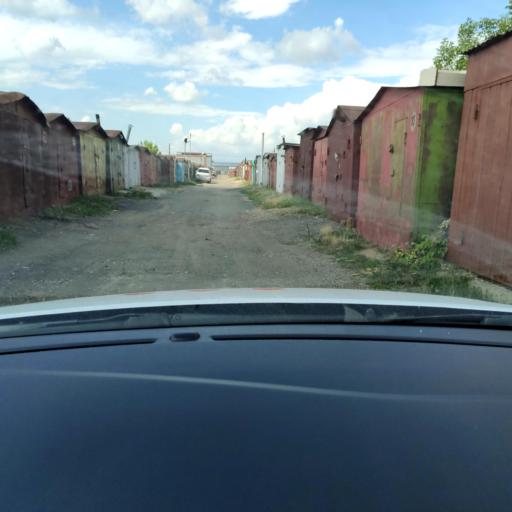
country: RU
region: Tatarstan
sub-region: Gorod Kazan'
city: Kazan
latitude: 55.8491
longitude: 49.1547
